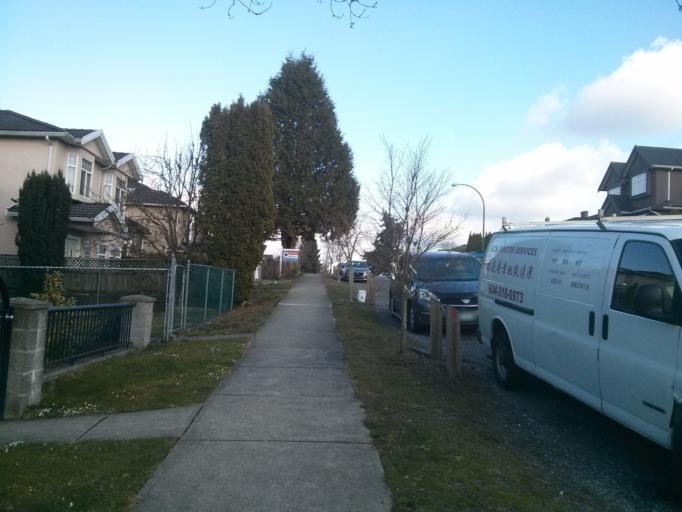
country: CA
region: British Columbia
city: Burnaby
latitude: 49.2454
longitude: -123.0270
